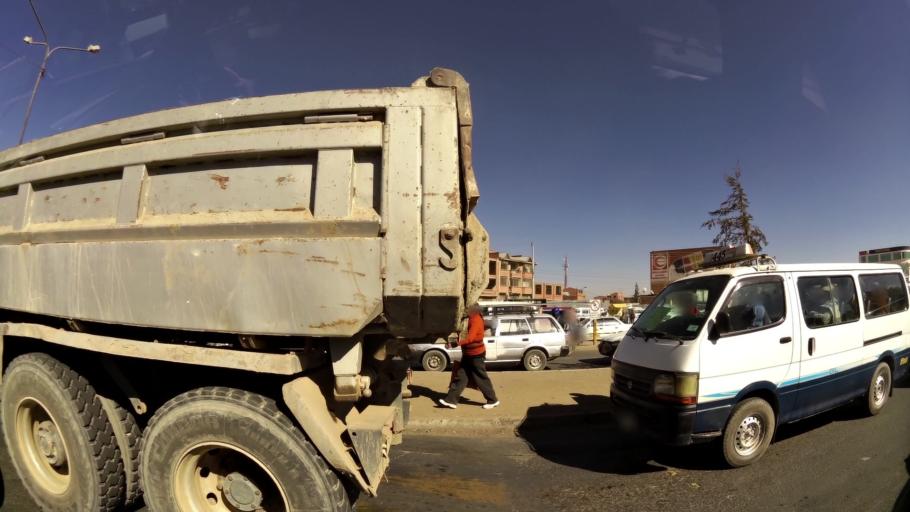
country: BO
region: La Paz
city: La Paz
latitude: -16.5811
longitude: -68.1852
